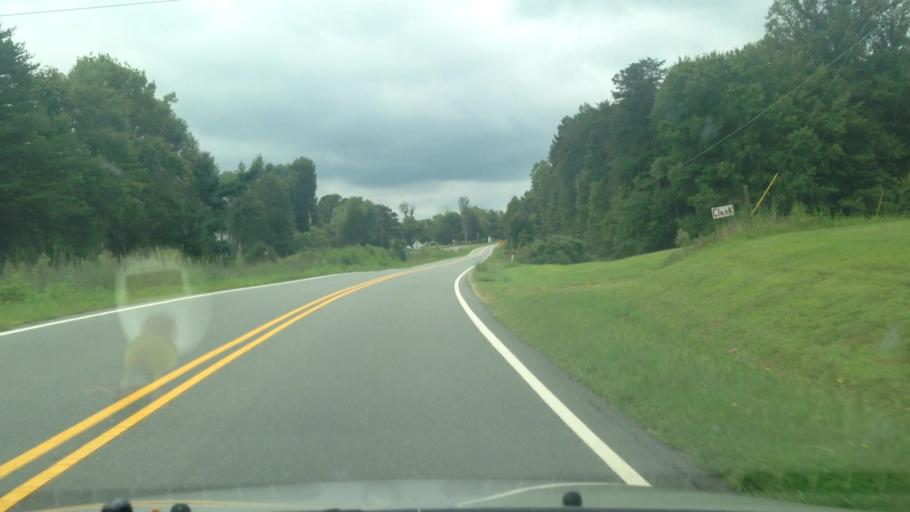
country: US
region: North Carolina
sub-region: Stokes County
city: Walnut Cove
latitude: 36.2418
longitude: -80.1537
